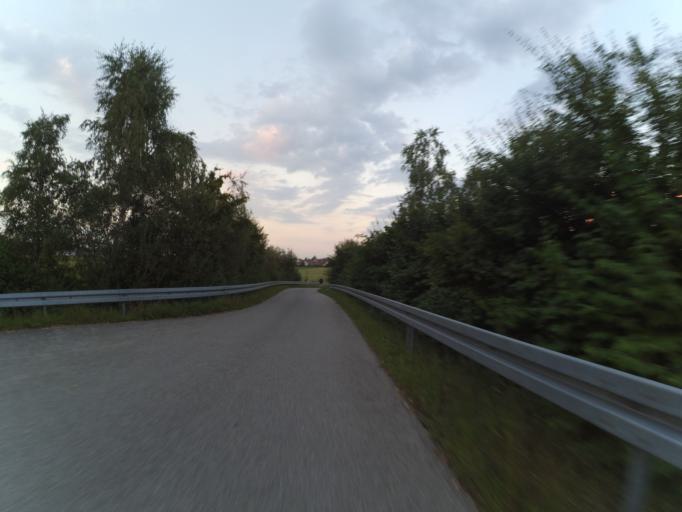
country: DE
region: Bavaria
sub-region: Swabia
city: Turkheim
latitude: 48.0582
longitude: 10.6266
